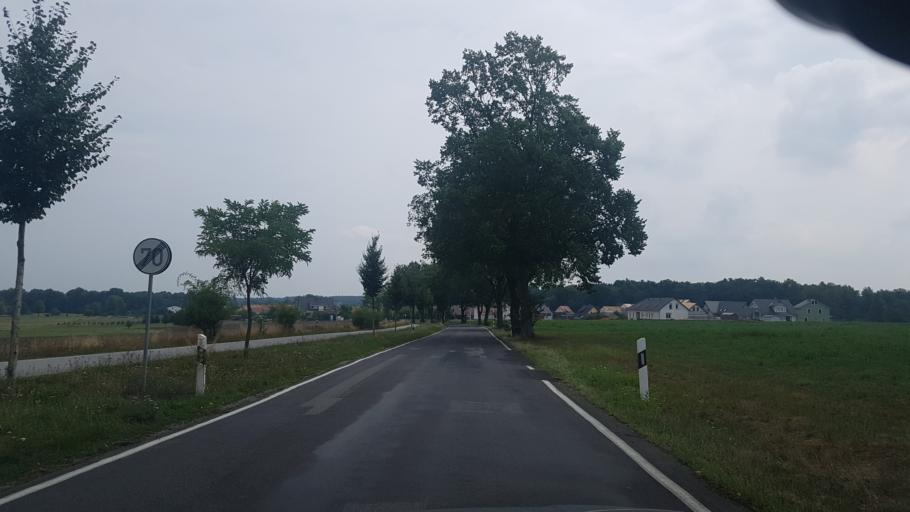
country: DE
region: Saxony
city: Horka
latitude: 51.2828
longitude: 14.2306
